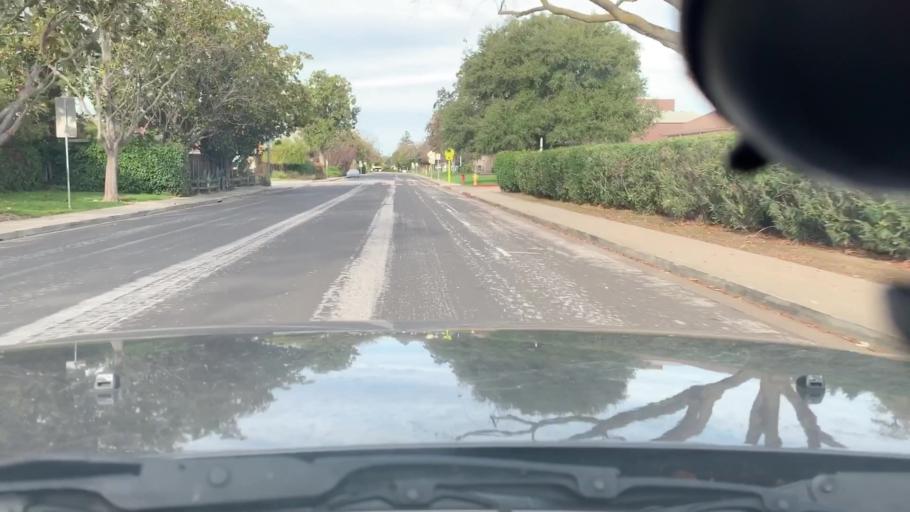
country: US
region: California
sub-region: Santa Clara County
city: Mountain View
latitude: 37.3588
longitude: -122.0687
